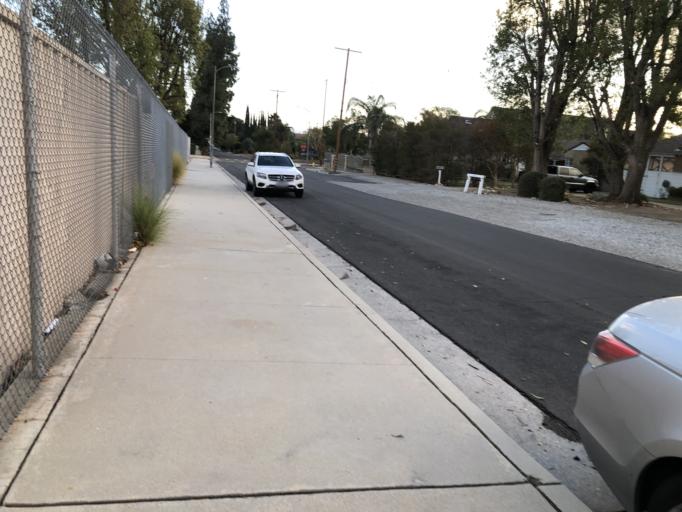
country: US
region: California
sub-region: Los Angeles County
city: Chatsworth
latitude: 34.2617
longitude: -118.5863
